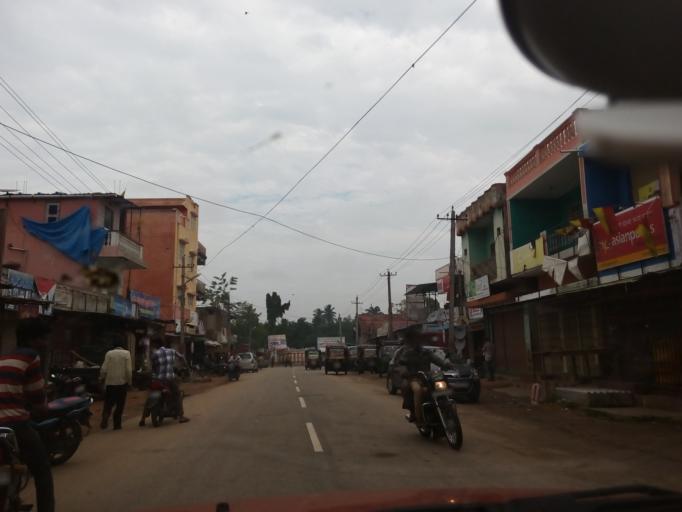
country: IN
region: Karnataka
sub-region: Hassan
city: Shravanabelagola
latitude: 12.8581
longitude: 76.4881
